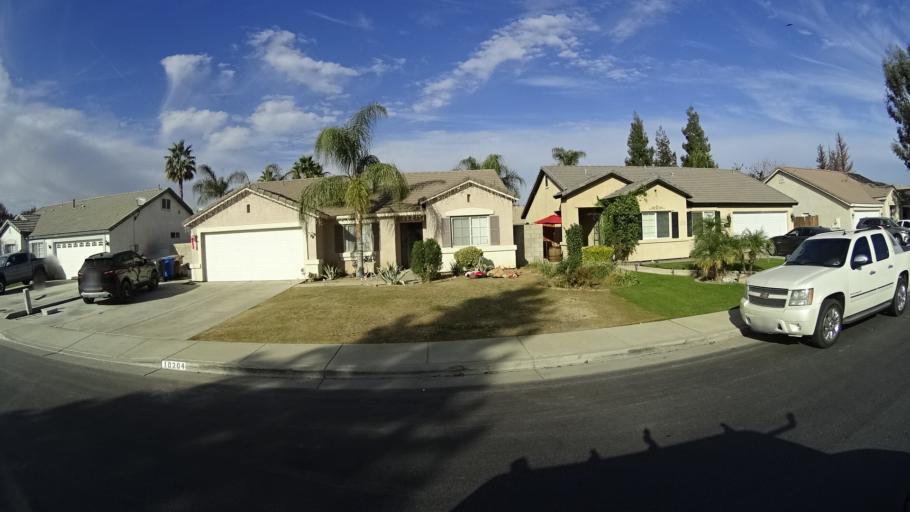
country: US
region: California
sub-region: Kern County
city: Greenacres
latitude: 35.3986
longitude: -119.1158
